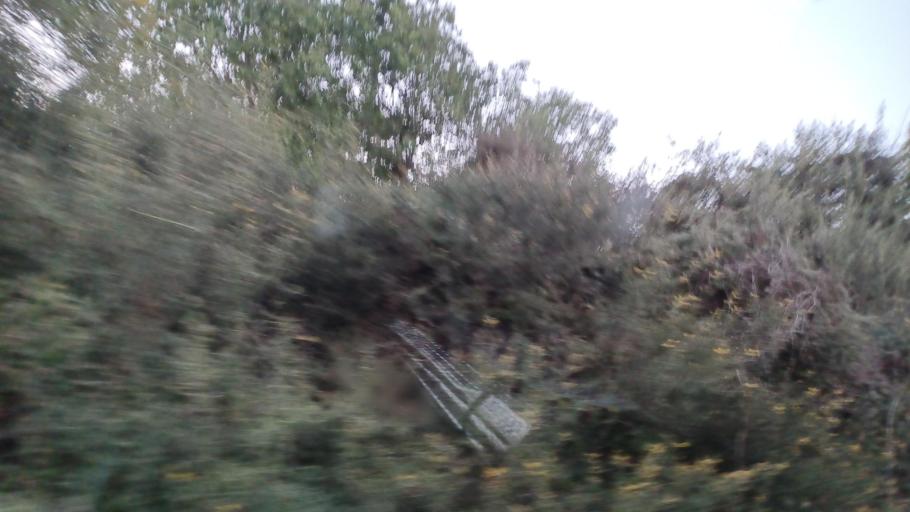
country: CY
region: Pafos
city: Mesogi
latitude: 34.8798
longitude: 32.4952
